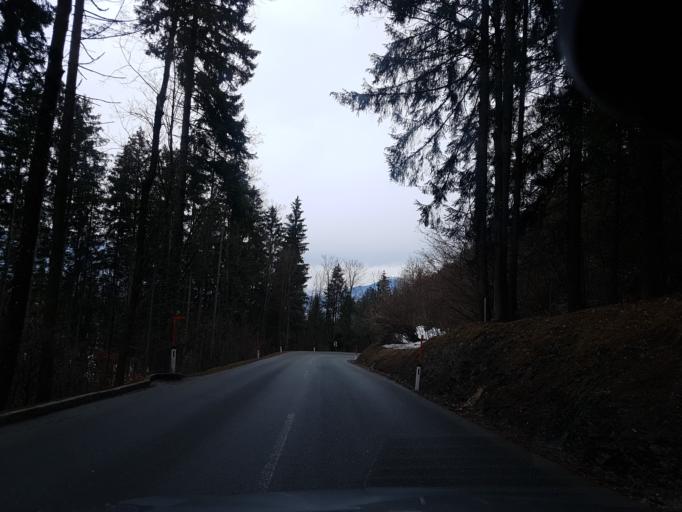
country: AT
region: Tyrol
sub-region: Politischer Bezirk Kufstein
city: Worgl
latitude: 47.4781
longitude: 12.0704
